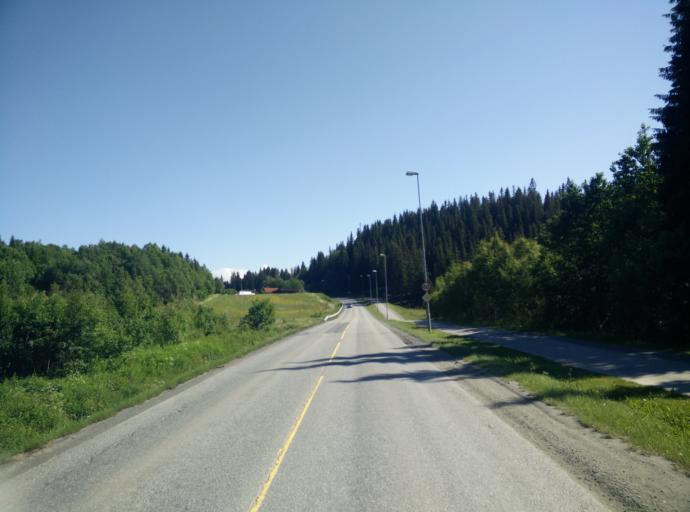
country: NO
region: Sor-Trondelag
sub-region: Trondheim
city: Trondheim
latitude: 63.3786
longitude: 10.3172
